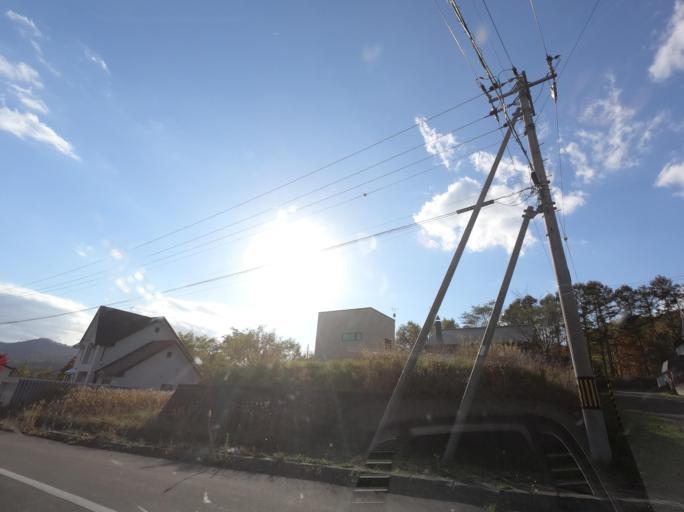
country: JP
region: Hokkaido
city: Iwamizawa
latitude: 42.9855
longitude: 141.9993
